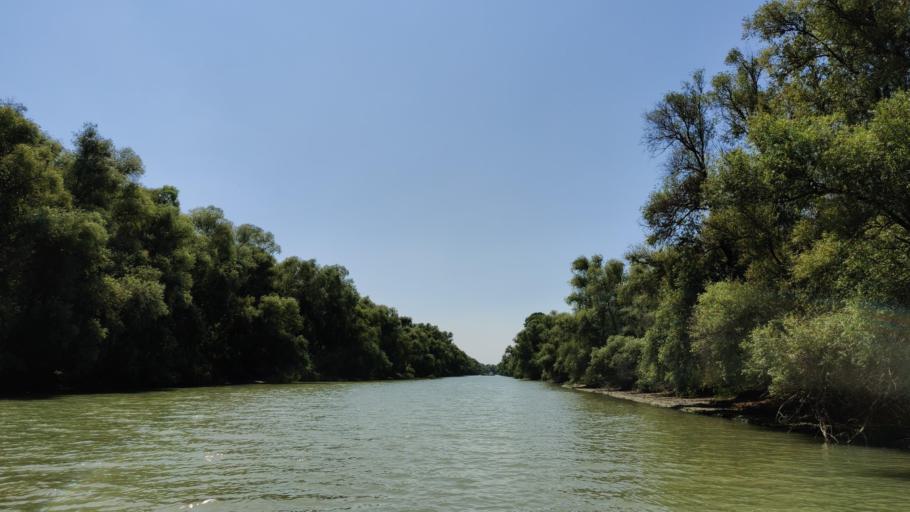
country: RO
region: Tulcea
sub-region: Comuna Pardina
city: Pardina
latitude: 45.2499
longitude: 28.9246
